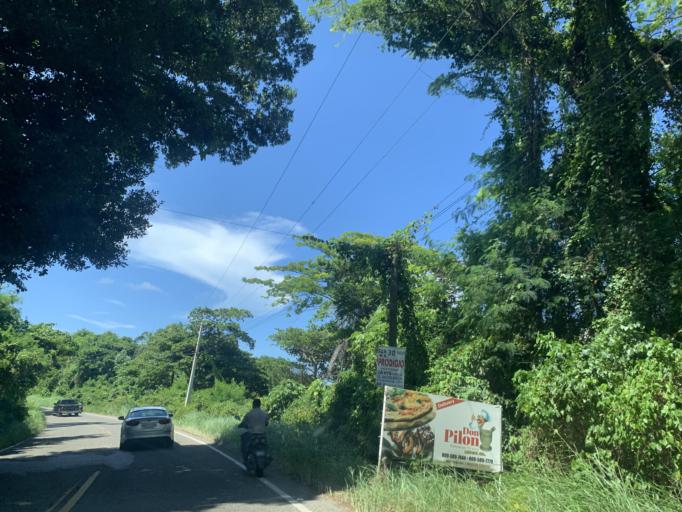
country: DO
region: Maria Trinidad Sanchez
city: Cabrera
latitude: 19.6596
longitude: -69.9383
